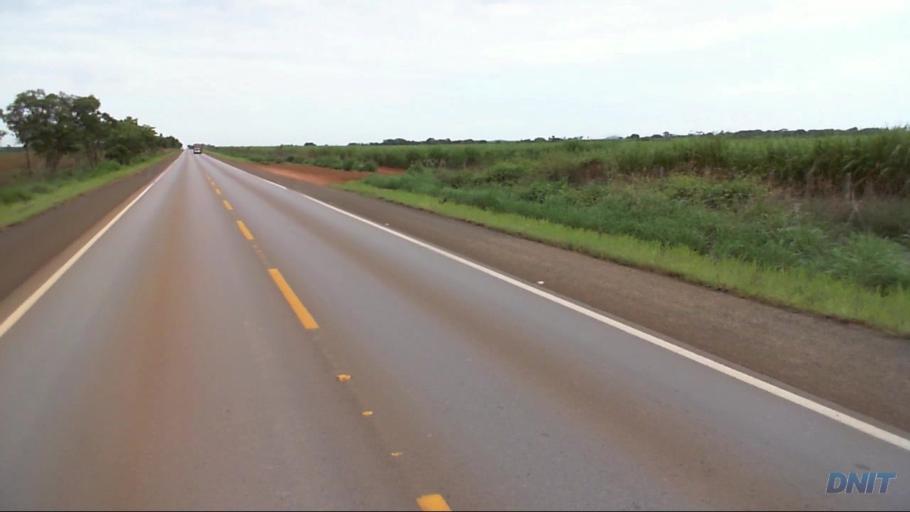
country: BR
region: Goias
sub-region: Uruacu
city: Uruacu
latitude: -14.7206
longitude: -49.1004
